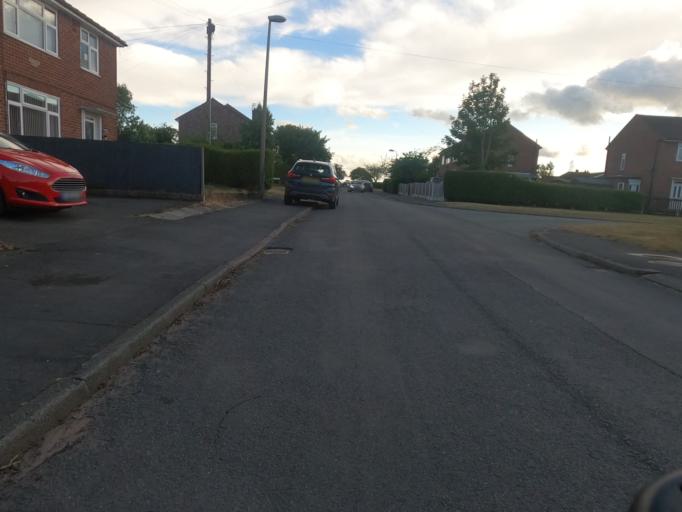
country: GB
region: England
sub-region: Cheshire West and Chester
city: Northwich
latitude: 53.2212
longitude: -2.5173
